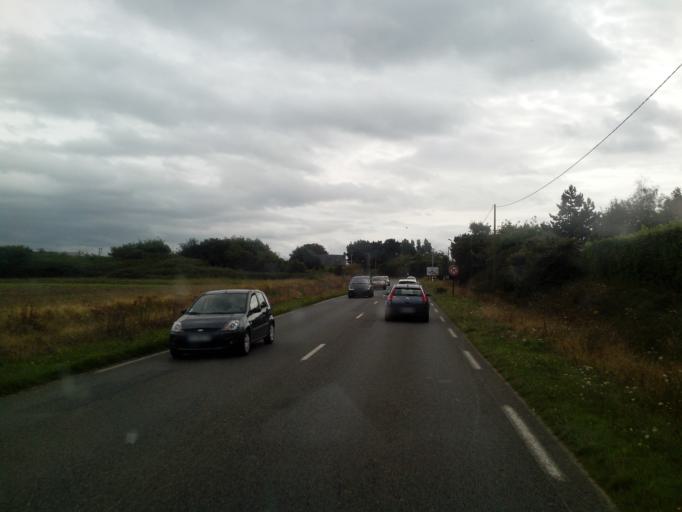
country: FR
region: Brittany
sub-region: Departement des Cotes-d'Armor
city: Etables-sur-Mer
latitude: 48.6213
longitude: -2.8259
